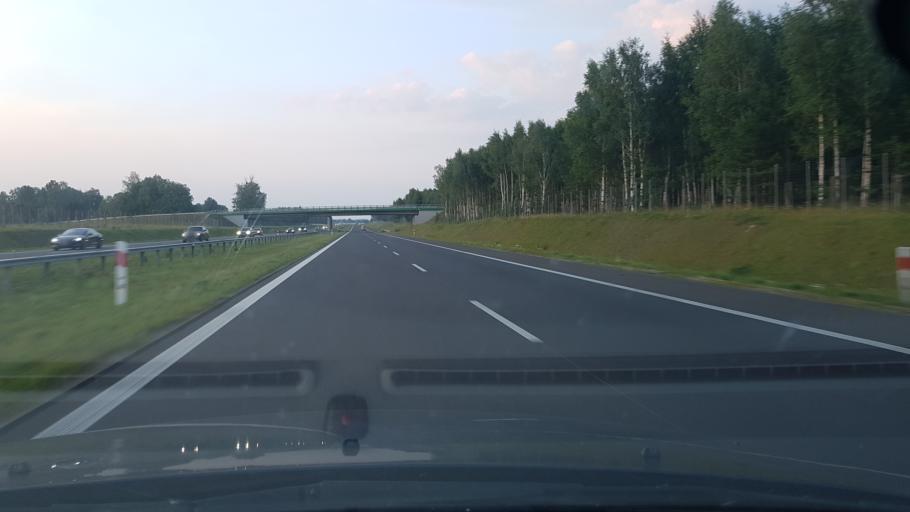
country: PL
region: Masovian Voivodeship
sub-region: Powiat mlawski
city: Wieczfnia Koscielna
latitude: 53.2612
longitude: 20.4275
